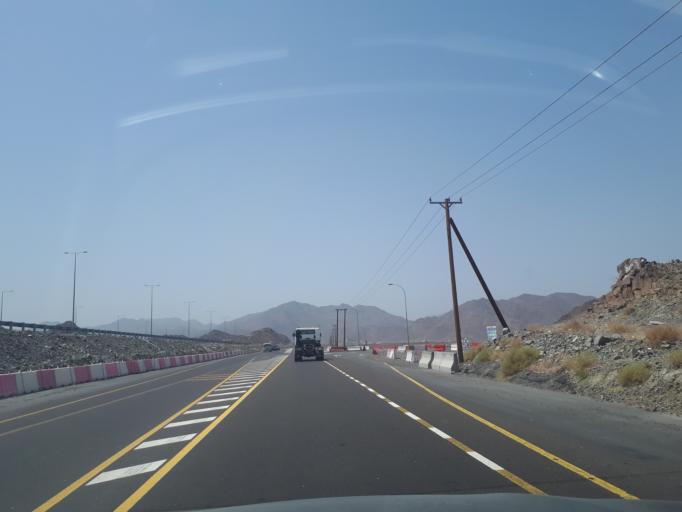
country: OM
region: Muhafazat ad Dakhiliyah
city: Sufalat Sama'il
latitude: 23.2846
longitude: 58.1081
